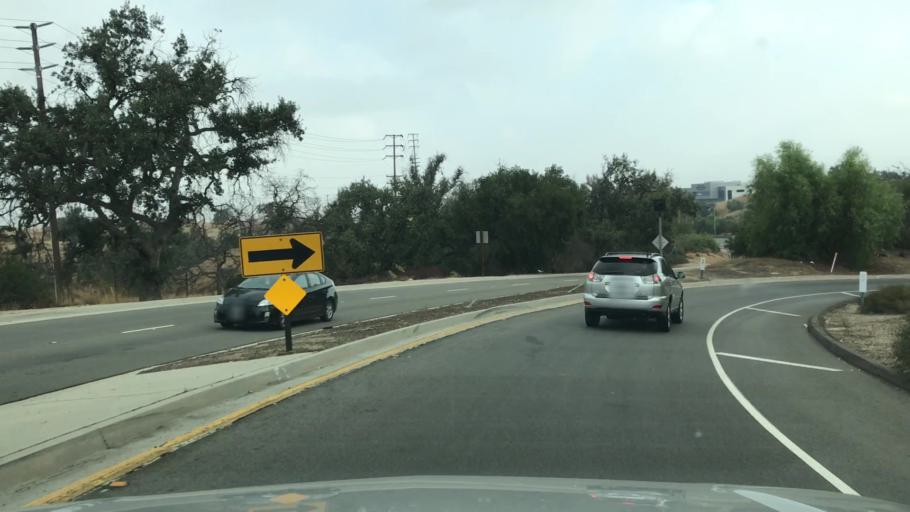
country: US
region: California
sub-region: Los Angeles County
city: Santa Clarita
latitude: 34.3944
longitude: -118.5727
